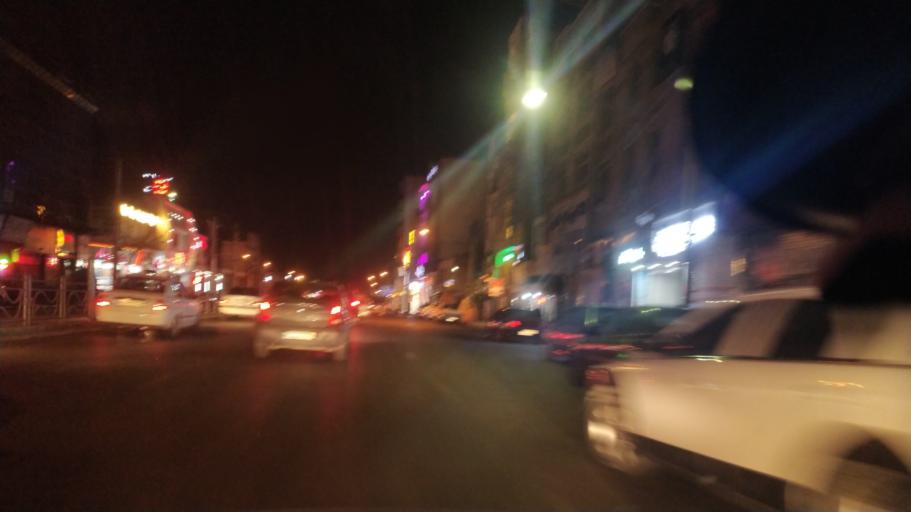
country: IR
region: Alborz
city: Karaj
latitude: 35.8153
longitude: 50.9979
